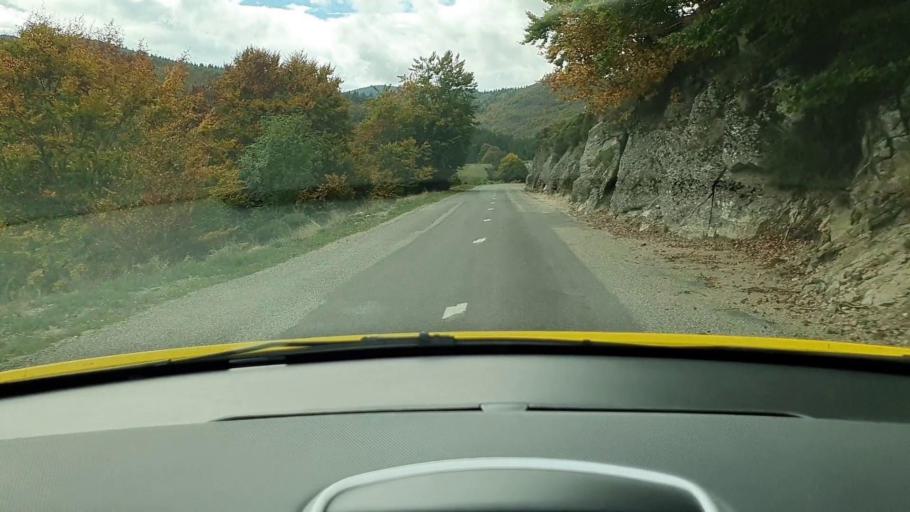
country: FR
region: Languedoc-Roussillon
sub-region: Departement de la Lozere
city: Meyrueis
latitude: 44.0757
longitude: 3.5005
